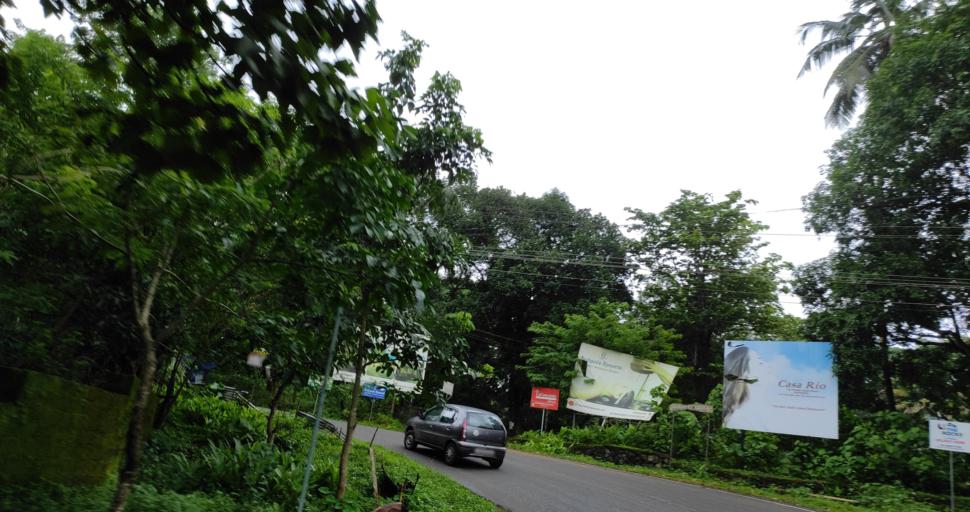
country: IN
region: Kerala
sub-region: Ernakulam
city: Angamali
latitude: 10.2870
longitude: 76.5562
